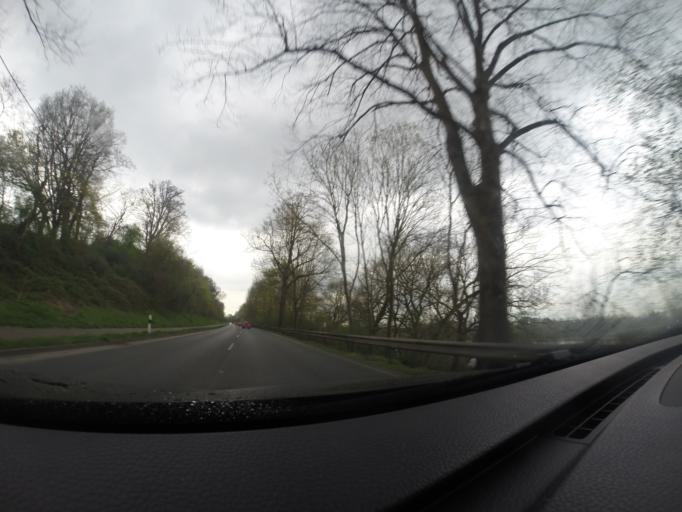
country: DE
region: North Rhine-Westphalia
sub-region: Regierungsbezirk Dusseldorf
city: Xanten
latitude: 51.6422
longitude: 6.4777
